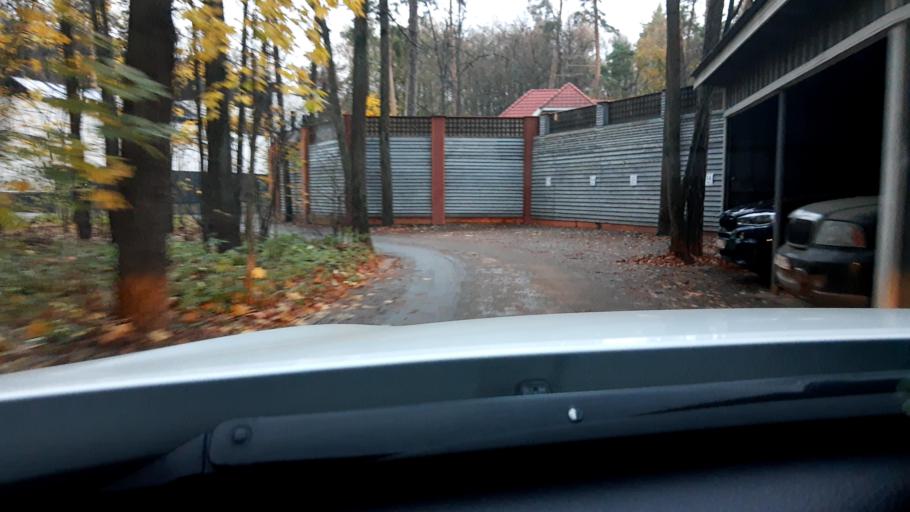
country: RU
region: Moscow
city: Strogino
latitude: 55.7835
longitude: 37.4146
